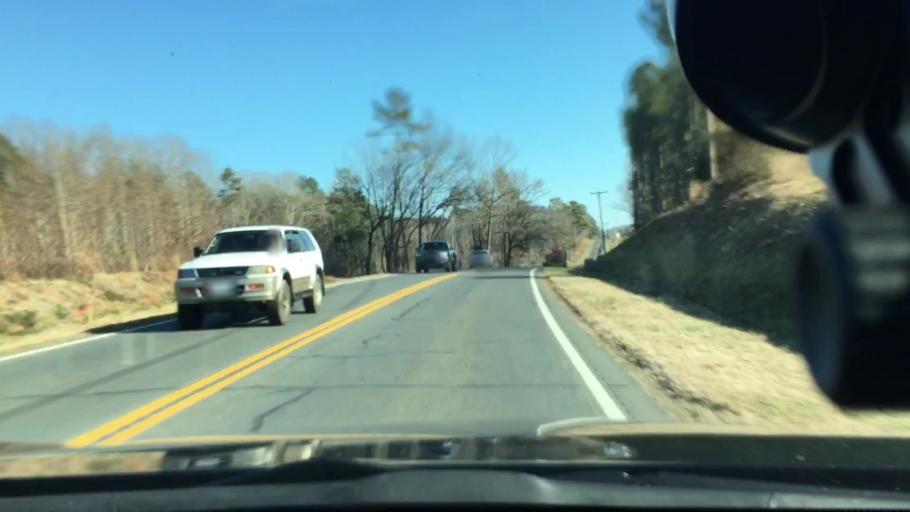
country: US
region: North Carolina
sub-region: Stanly County
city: Badin
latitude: 35.3169
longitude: -80.1091
